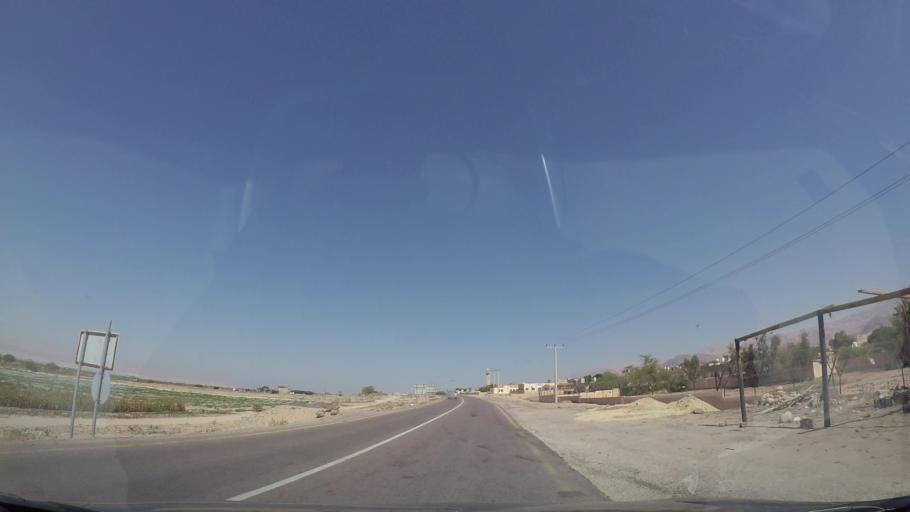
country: JO
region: Karak
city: Safi
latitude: 30.9167
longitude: 35.4584
